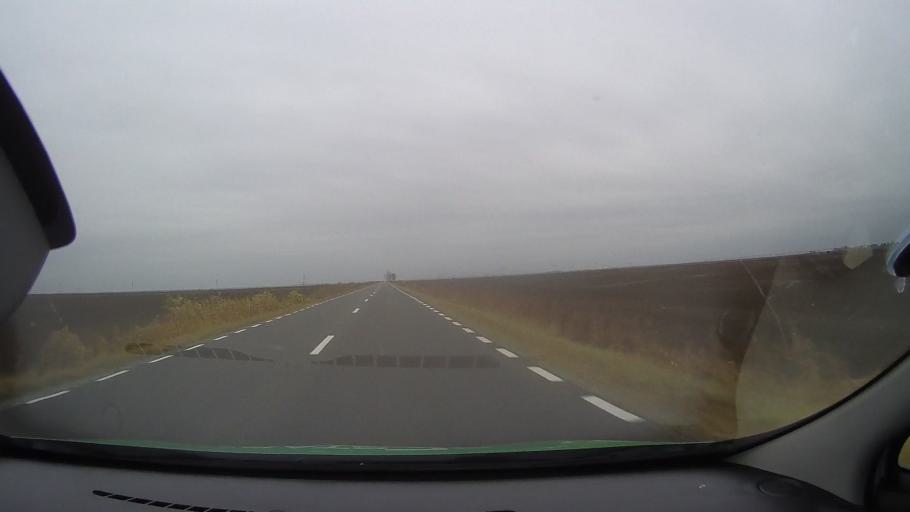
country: RO
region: Ialomita
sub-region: Comuna Gheorghe Lazar
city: Gheorghe Lazar
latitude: 44.6642
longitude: 27.4148
